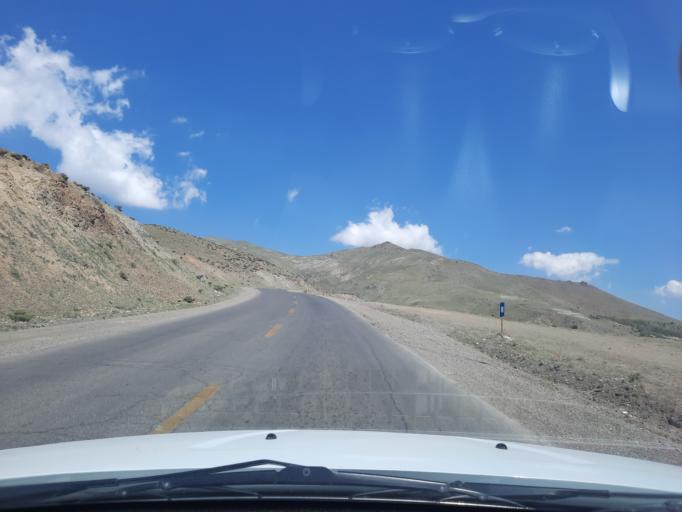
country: IR
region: Qazvin
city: Qazvin
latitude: 36.3573
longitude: 50.1917
